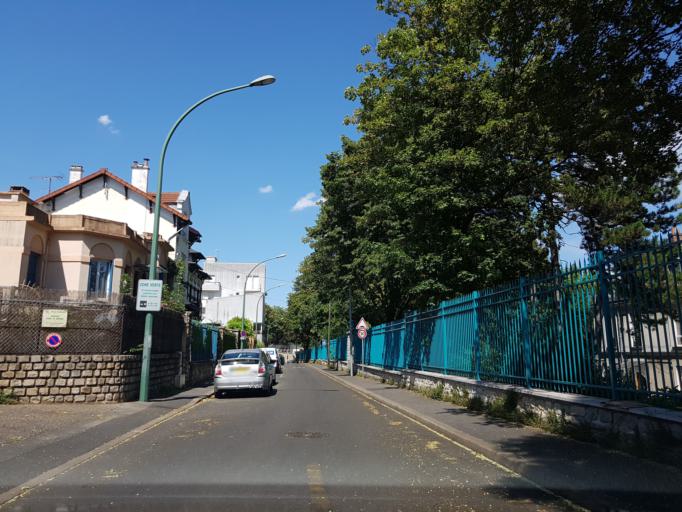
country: FR
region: Ile-de-France
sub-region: Departement du Val-de-Marne
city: Arcueil
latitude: 48.8026
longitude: 2.3296
